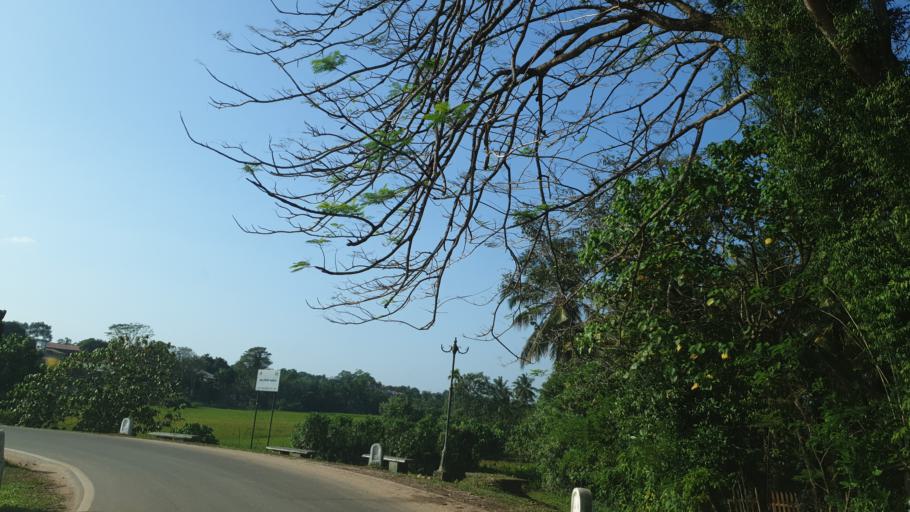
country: LK
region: Western
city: Battaramulla South
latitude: 6.8892
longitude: 79.9477
